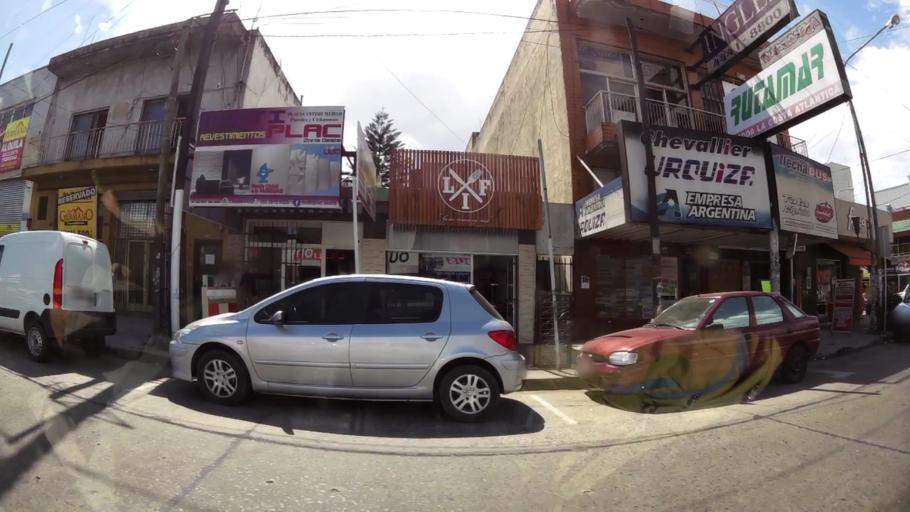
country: AR
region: Buenos Aires
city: San Justo
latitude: -34.6760
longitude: -58.5644
